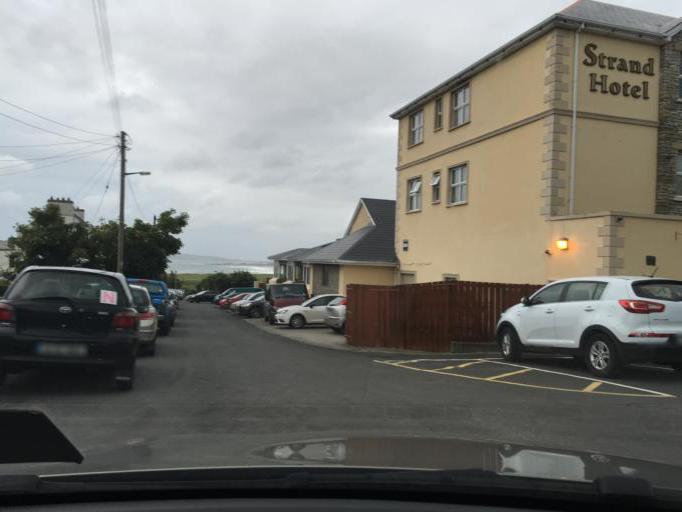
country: IE
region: Ulster
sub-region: County Donegal
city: Carndonagh
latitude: 55.2807
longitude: -7.3937
